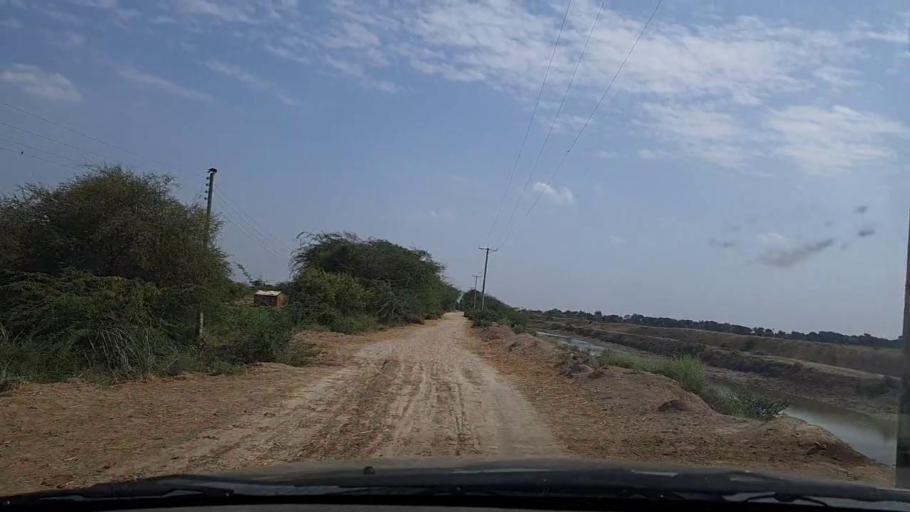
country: PK
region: Sindh
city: Mirpur Batoro
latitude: 24.5667
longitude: 68.1986
